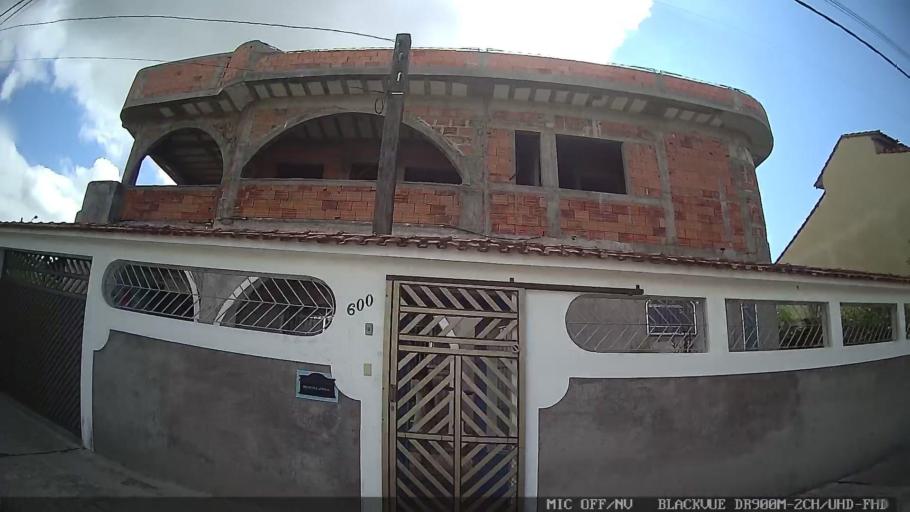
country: BR
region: Sao Paulo
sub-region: Peruibe
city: Peruibe
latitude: -24.3128
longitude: -47.0073
